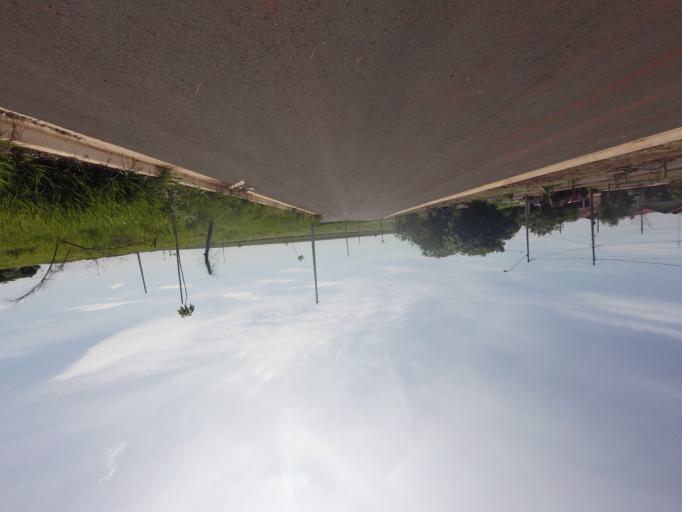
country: BR
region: Sao Paulo
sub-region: Piracicaba
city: Piracicaba
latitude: -22.7581
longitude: -47.5795
